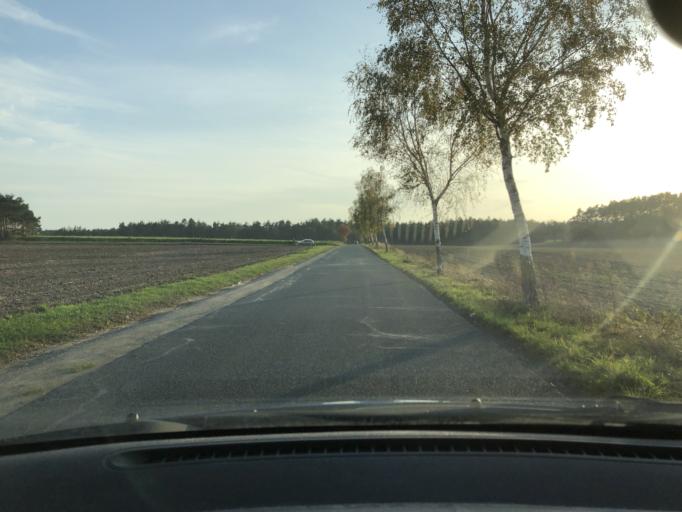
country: DE
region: Lower Saxony
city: Hitzacker
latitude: 53.1342
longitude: 11.0292
